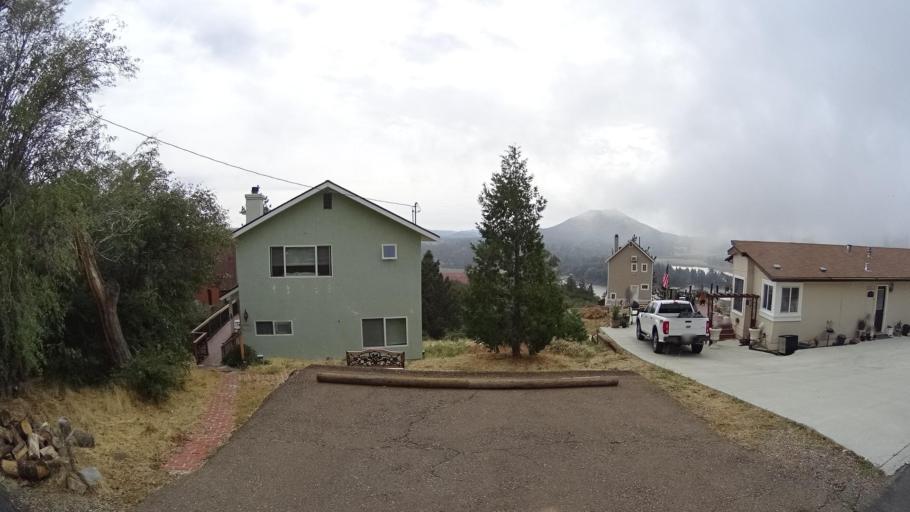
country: US
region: California
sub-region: San Diego County
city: Julian
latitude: 32.9951
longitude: -116.5797
